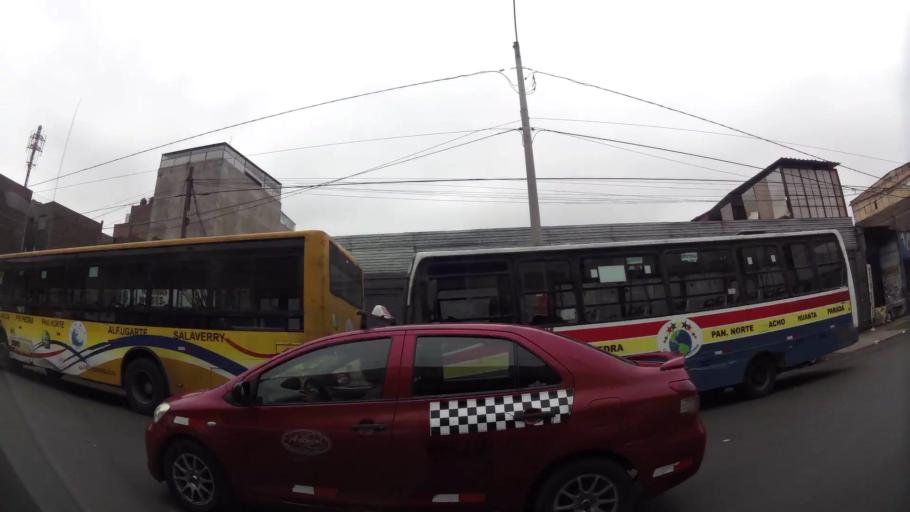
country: PE
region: Lima
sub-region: Lima
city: San Luis
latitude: -12.0731
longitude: -77.0115
